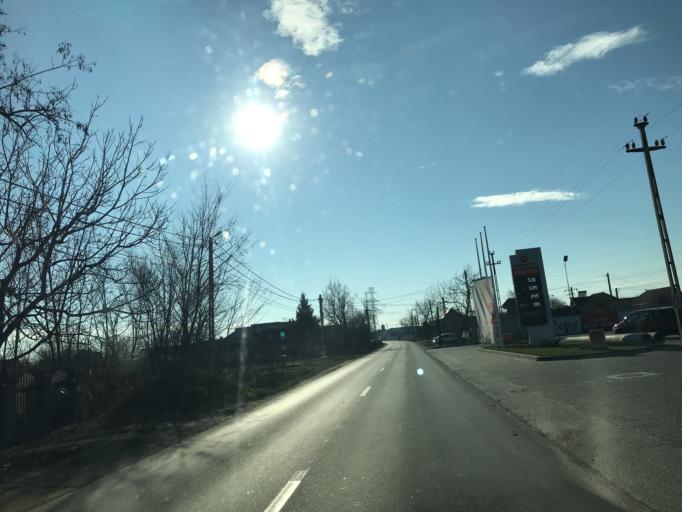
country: RO
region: Olt
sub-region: Comuna Slatioara
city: Slatioara
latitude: 44.4152
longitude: 24.3265
